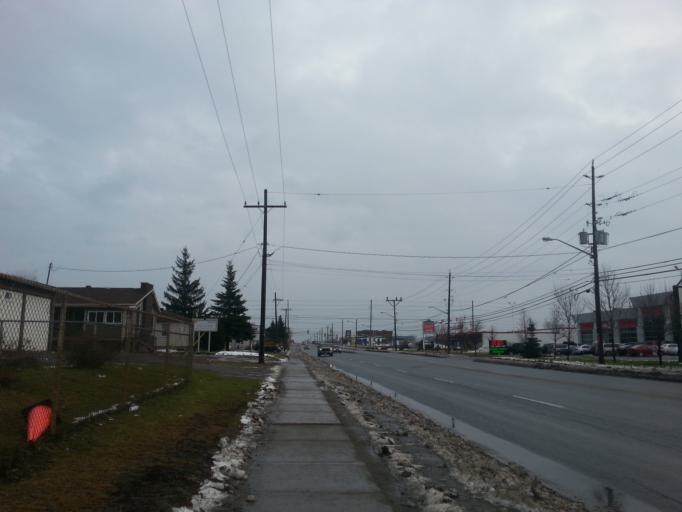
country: CA
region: Ontario
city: Greater Sudbury
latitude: 46.5221
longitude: -80.9263
